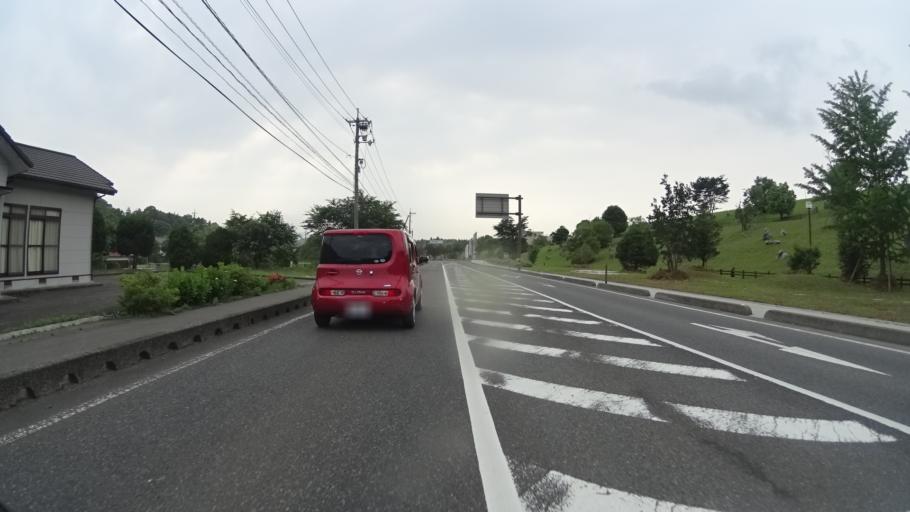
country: JP
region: Yamaguchi
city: Nagato
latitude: 34.1959
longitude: 131.1349
